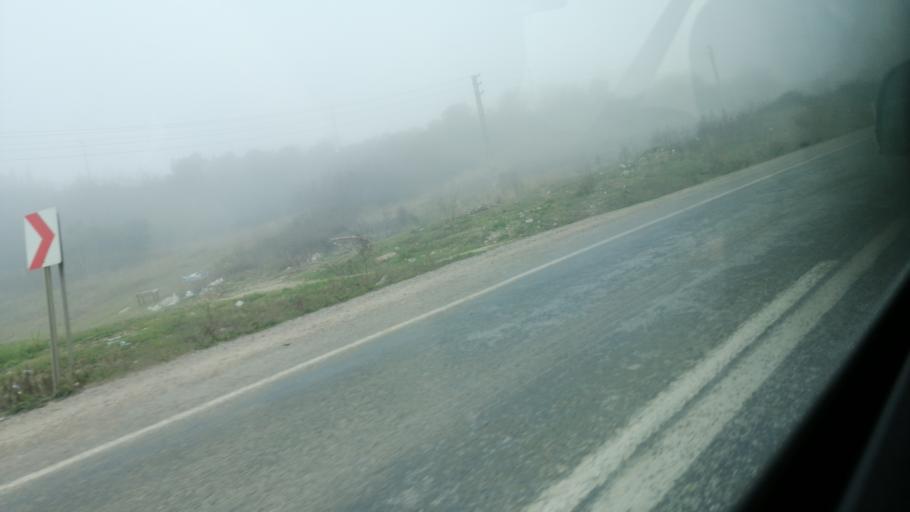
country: TR
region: Yalova
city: Kadikoy
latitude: 40.6500
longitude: 29.2021
